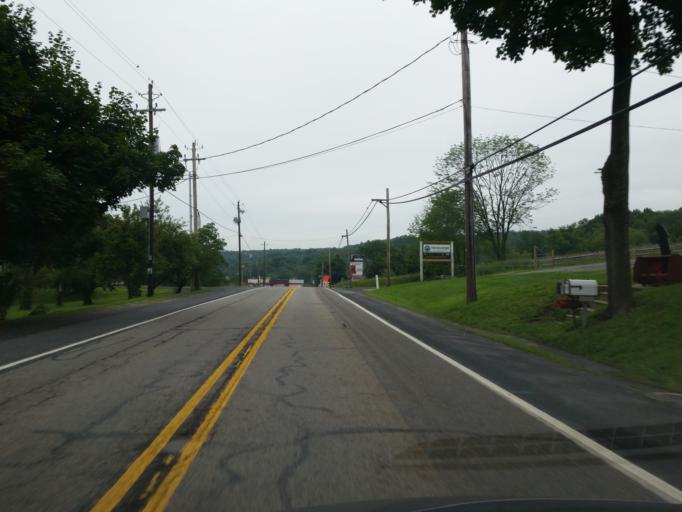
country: US
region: Pennsylvania
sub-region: Schuylkill County
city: Pine Grove
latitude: 40.5355
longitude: -76.4210
